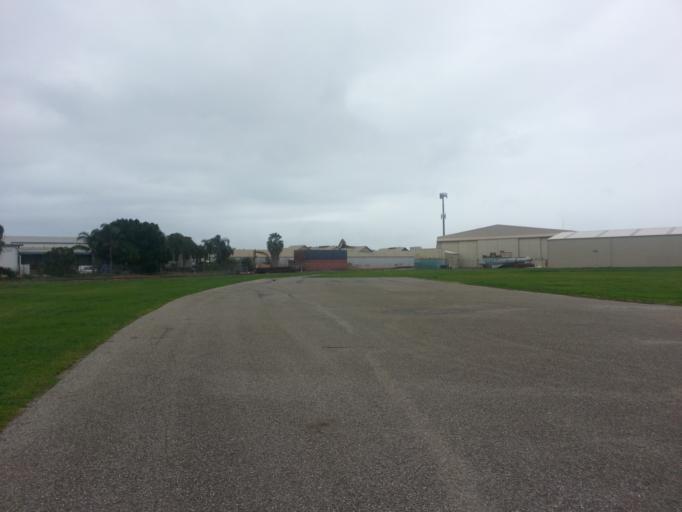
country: AU
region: South Australia
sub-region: Port Adelaide Enfield
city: Alberton
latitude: -34.8489
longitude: 138.5131
